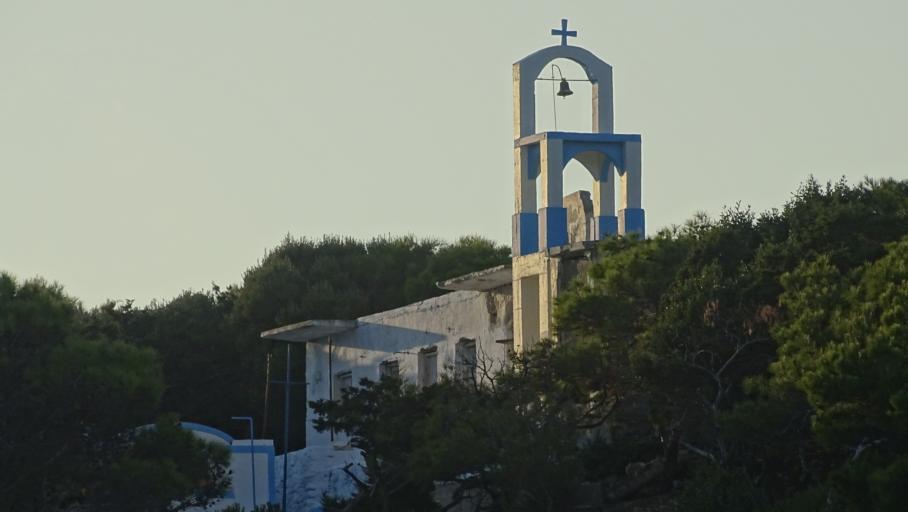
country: GR
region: South Aegean
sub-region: Nomos Dodekanisou
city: Kalymnos
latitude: 36.9133
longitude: 26.9426
